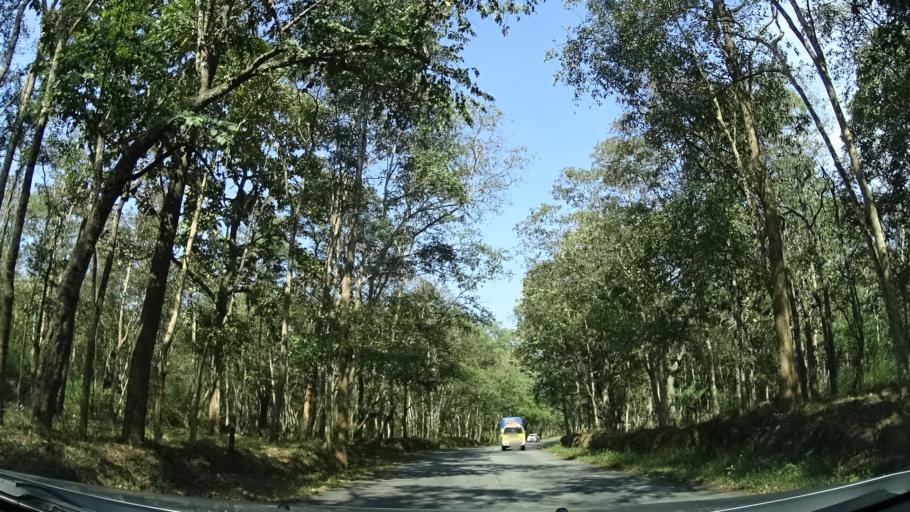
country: IN
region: Tamil Nadu
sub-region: Nilgiri
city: Naduvattam
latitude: 11.7107
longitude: 76.4167
